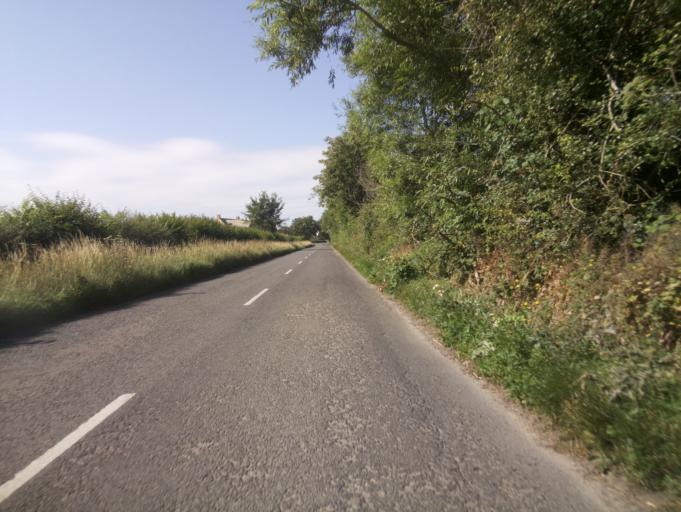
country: GB
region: England
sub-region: Oxfordshire
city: Bampton
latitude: 51.7304
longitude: -1.5063
